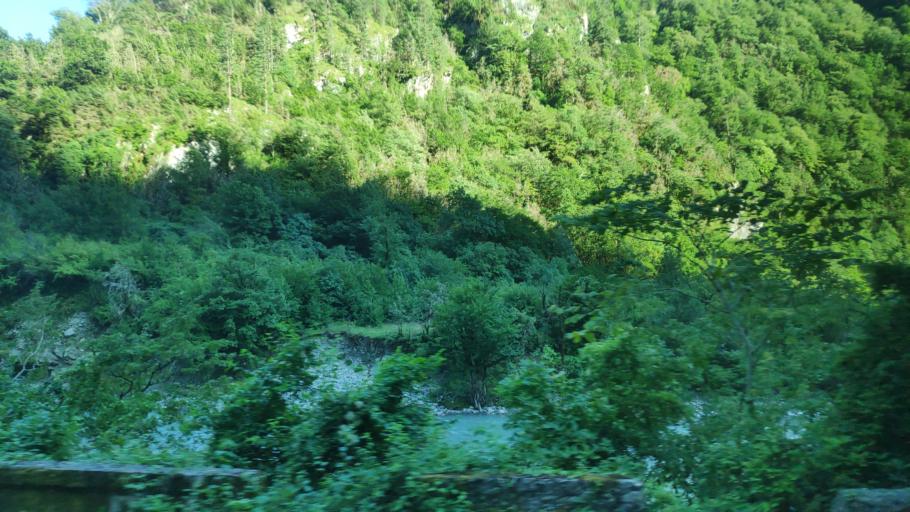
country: GE
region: Abkhazia
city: Gagra
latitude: 43.3683
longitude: 40.4572
